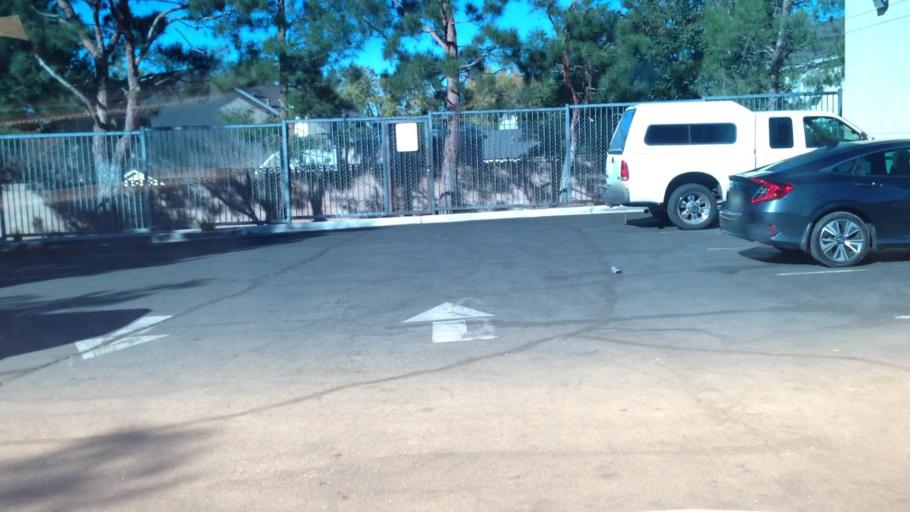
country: US
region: California
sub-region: Los Angeles County
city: Quartz Hill
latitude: 34.6609
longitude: -118.1844
